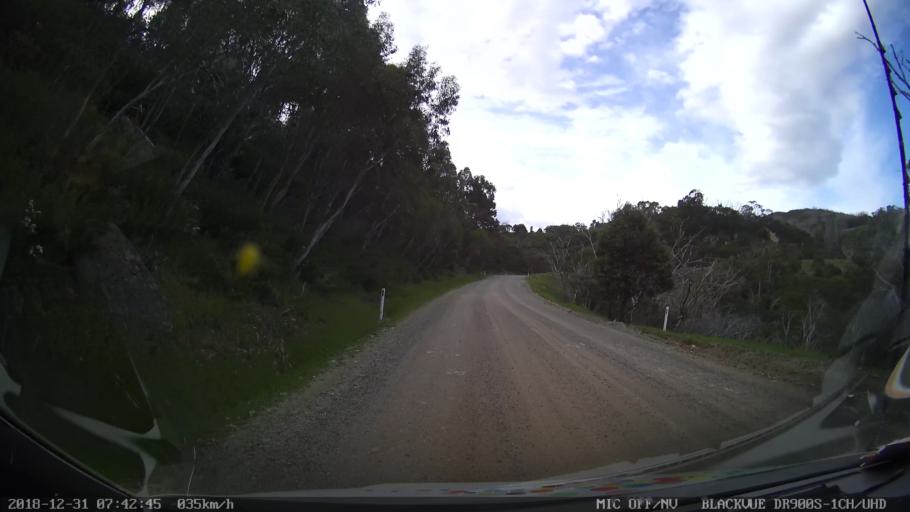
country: AU
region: New South Wales
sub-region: Snowy River
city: Jindabyne
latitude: -36.3580
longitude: 148.4081
